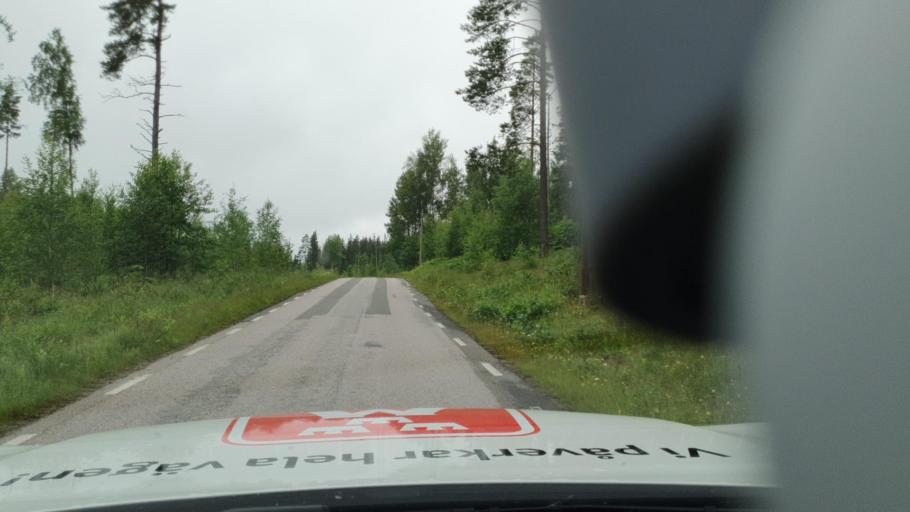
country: SE
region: Vaestra Goetaland
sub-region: Gullspangs Kommun
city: Gullspang
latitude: 59.0369
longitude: 14.1574
